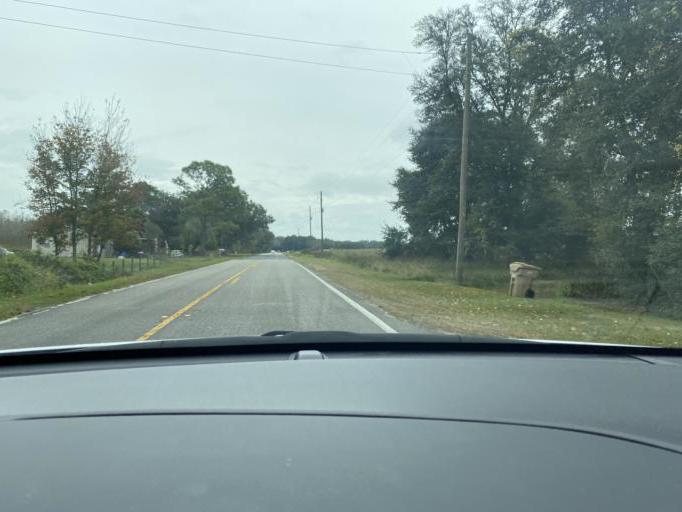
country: US
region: Florida
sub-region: Lake County
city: Groveland
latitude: 28.4121
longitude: -81.8285
